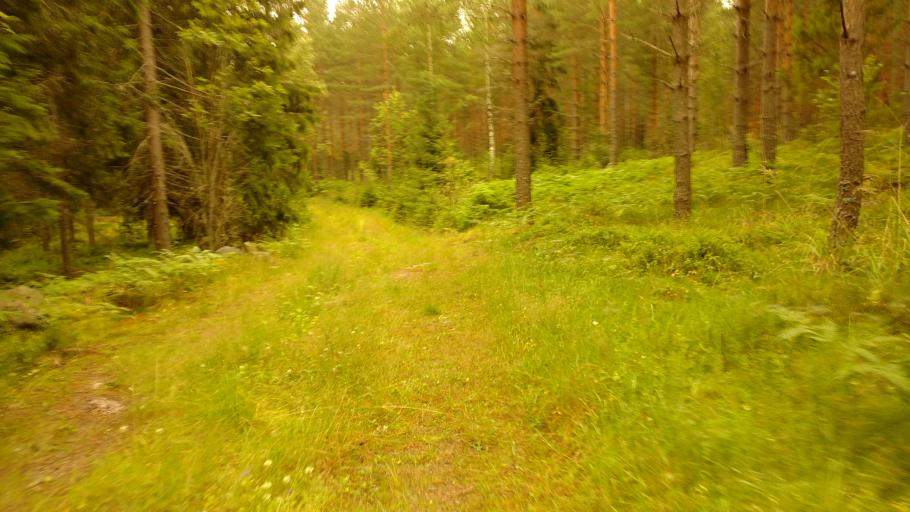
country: FI
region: Varsinais-Suomi
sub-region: Salo
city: Pertteli
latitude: 60.4089
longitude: 23.2289
